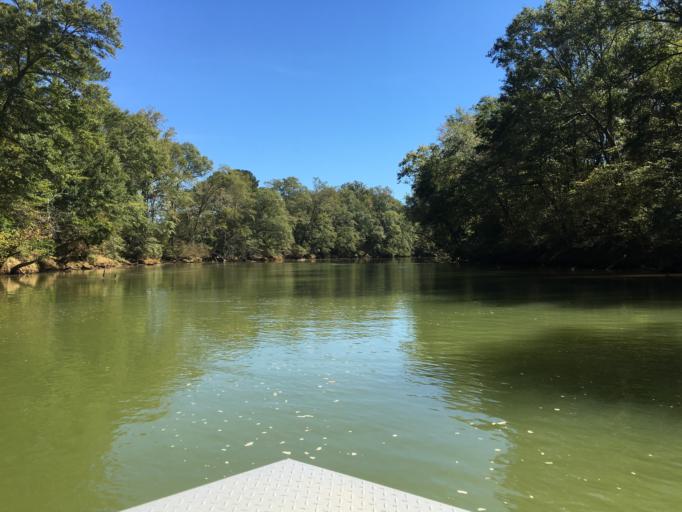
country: US
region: Georgia
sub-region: Fulton County
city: Johns Creek
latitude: 34.0039
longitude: -84.2139
